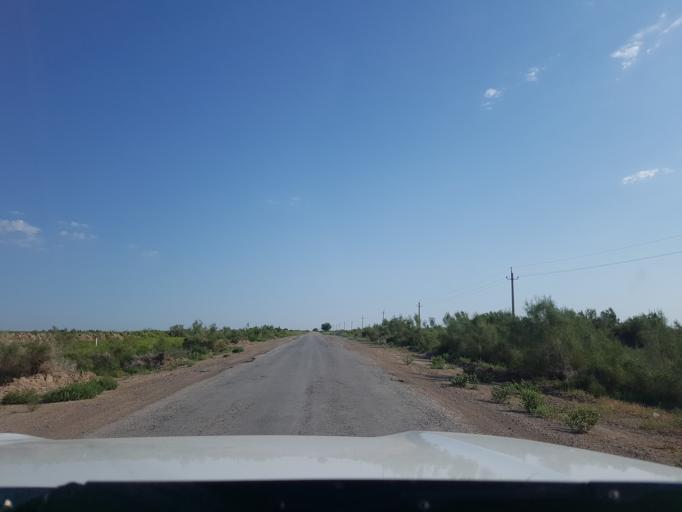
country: TM
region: Dasoguz
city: Koeneuergench
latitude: 41.9176
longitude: 58.7111
